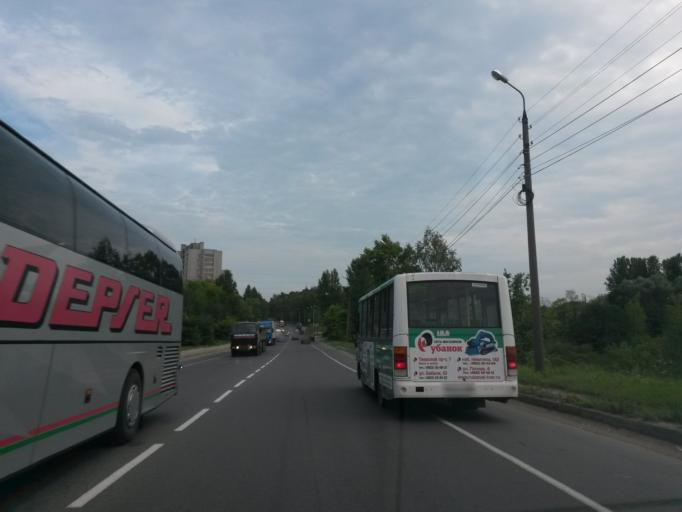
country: RU
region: Jaroslavl
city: Yaroslavl
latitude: 57.5874
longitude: 39.8201
